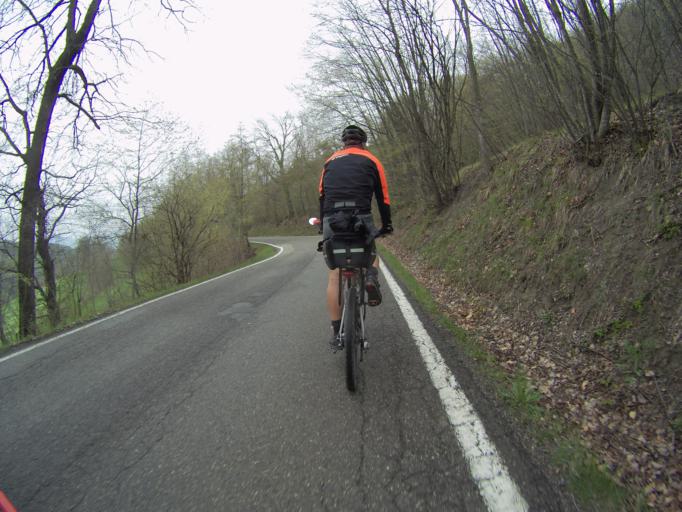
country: IT
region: Emilia-Romagna
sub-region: Provincia di Reggio Emilia
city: Casina
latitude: 44.5460
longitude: 10.4601
